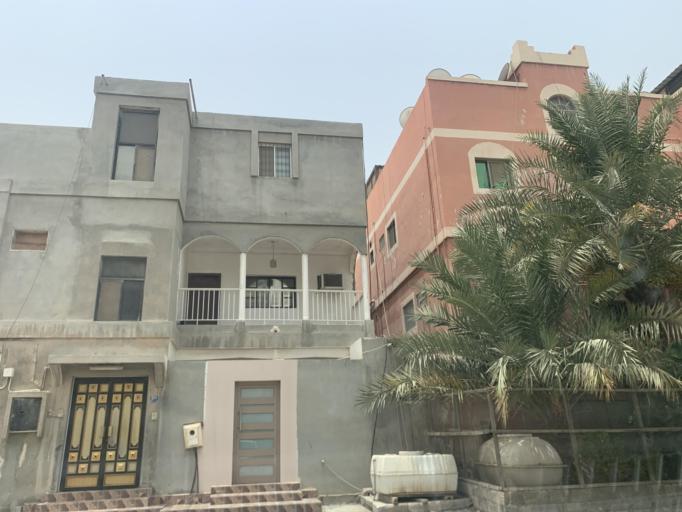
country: BH
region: Manama
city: Jidd Hafs
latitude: 26.2153
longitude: 50.5006
